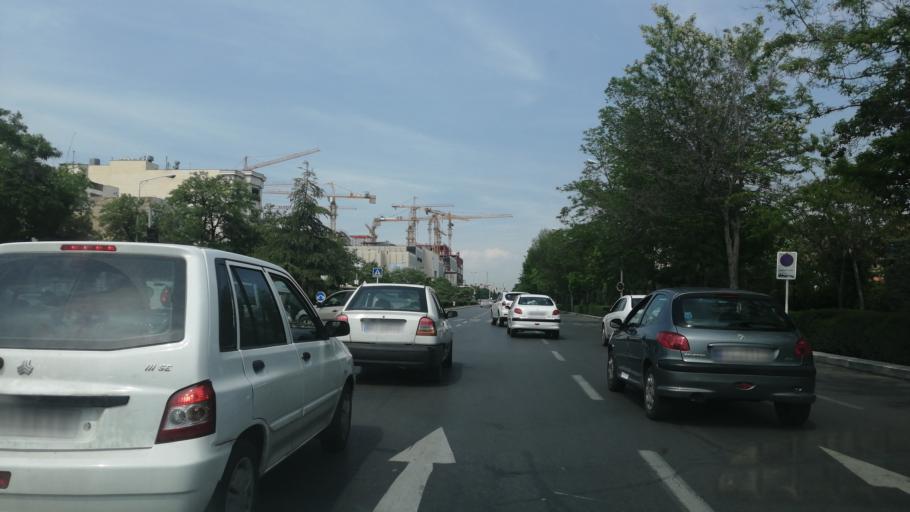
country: IR
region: Razavi Khorasan
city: Mashhad
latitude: 36.3131
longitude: 59.5584
